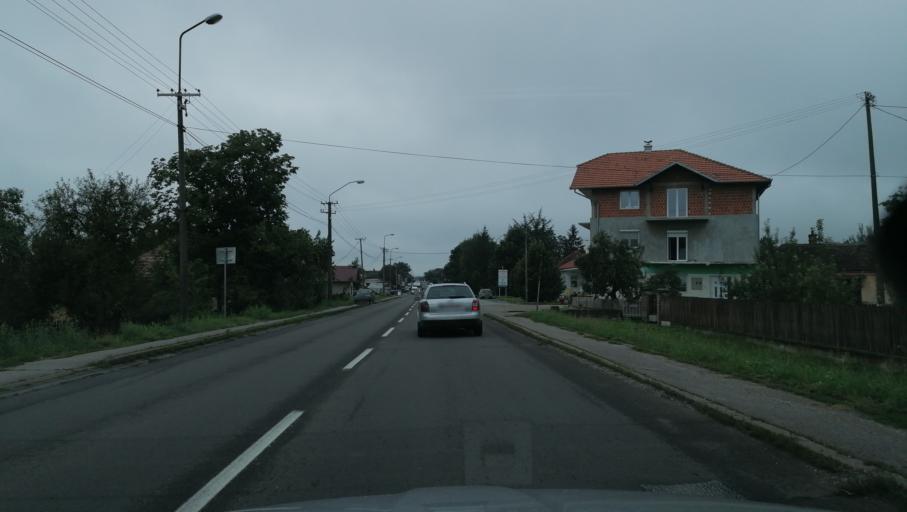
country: RS
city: Prislonica
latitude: 43.8651
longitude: 20.5365
